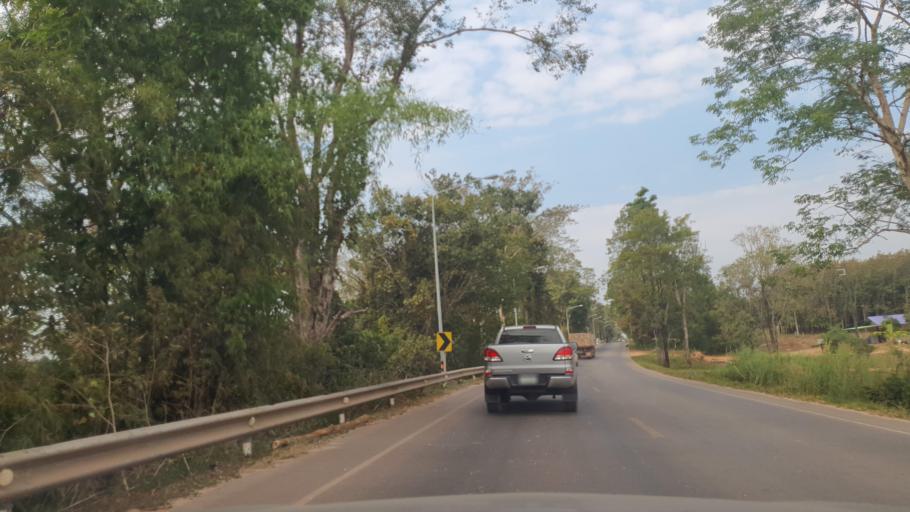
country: TH
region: Changwat Bueng Kan
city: Si Wilai
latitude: 18.2741
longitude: 103.8332
